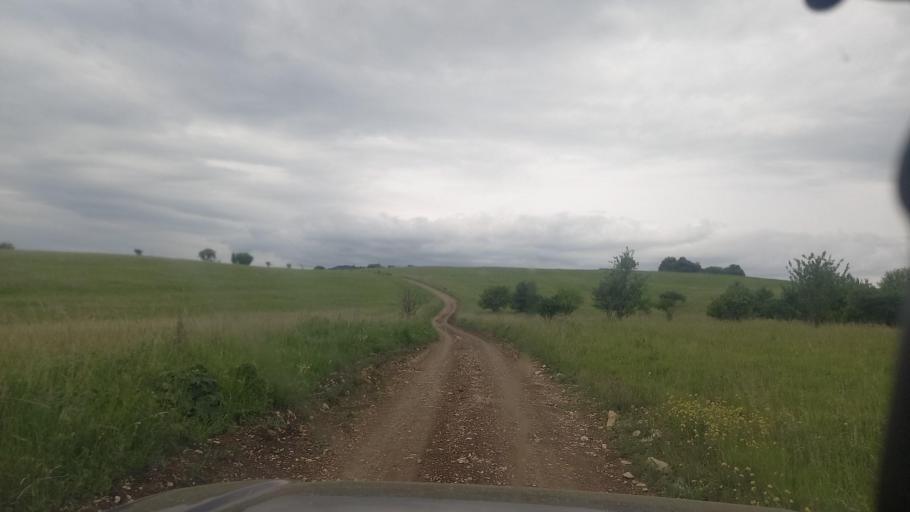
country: RU
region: Krasnodarskiy
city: Peredovaya
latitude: 44.0719
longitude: 41.3633
